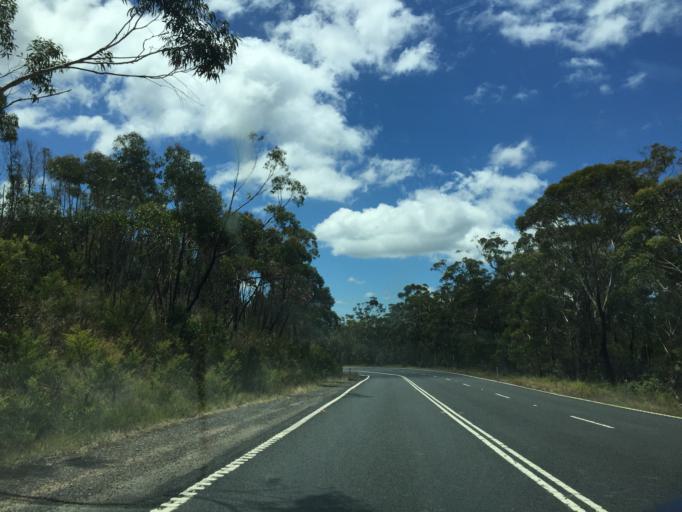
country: AU
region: New South Wales
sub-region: Blue Mountains Municipality
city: Blackheath
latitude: -33.5595
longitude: 150.3435
